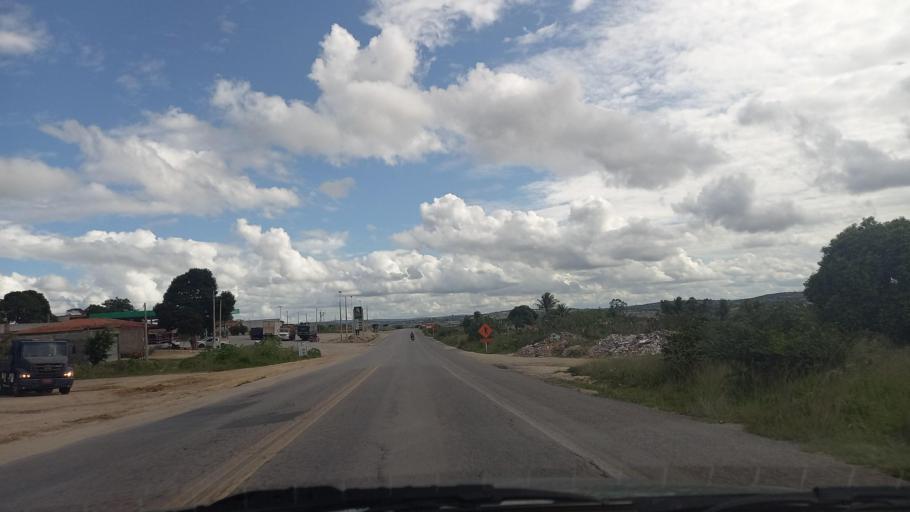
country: BR
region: Pernambuco
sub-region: Lajedo
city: Lajedo
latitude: -8.7192
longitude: -36.4242
